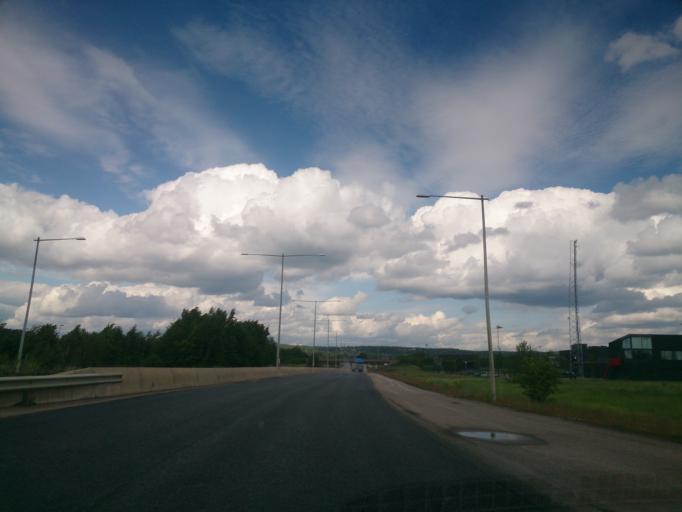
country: SE
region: OEstergoetland
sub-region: Norrkopings Kommun
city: Jursla
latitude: 58.6462
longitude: 16.1638
